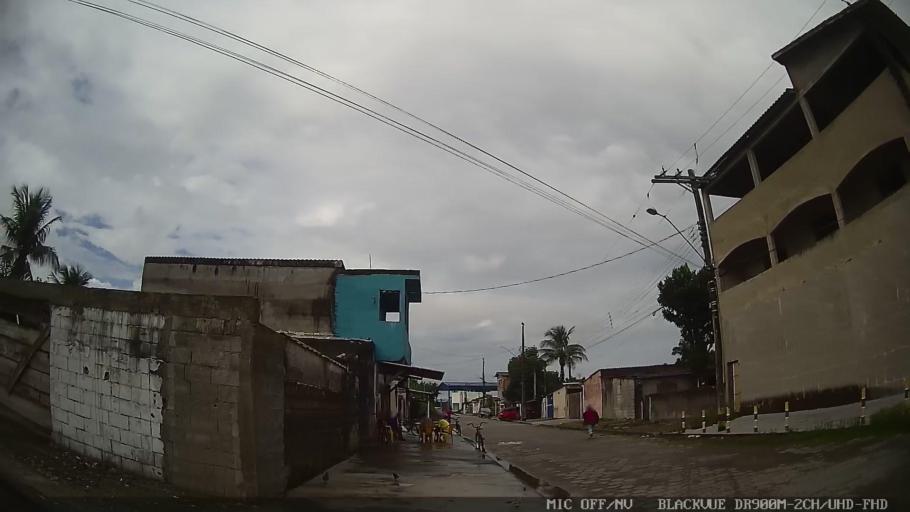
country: BR
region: Sao Paulo
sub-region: Itanhaem
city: Itanhaem
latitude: -24.1607
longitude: -46.7974
